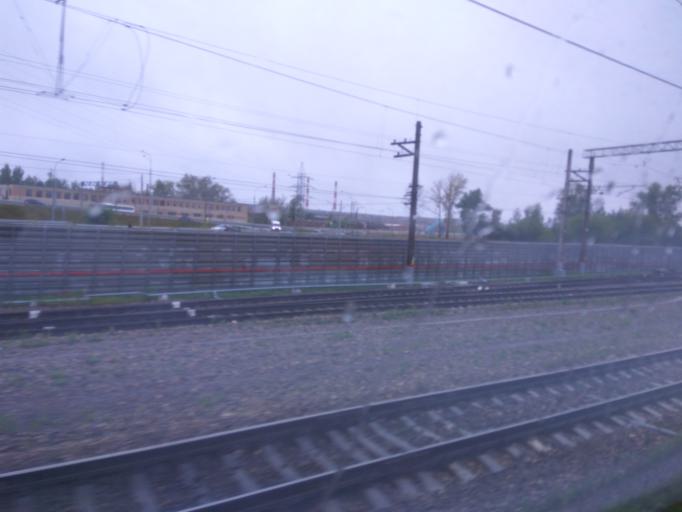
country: RU
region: Moskovskaya
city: Stupino
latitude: 54.9063
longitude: 38.0814
